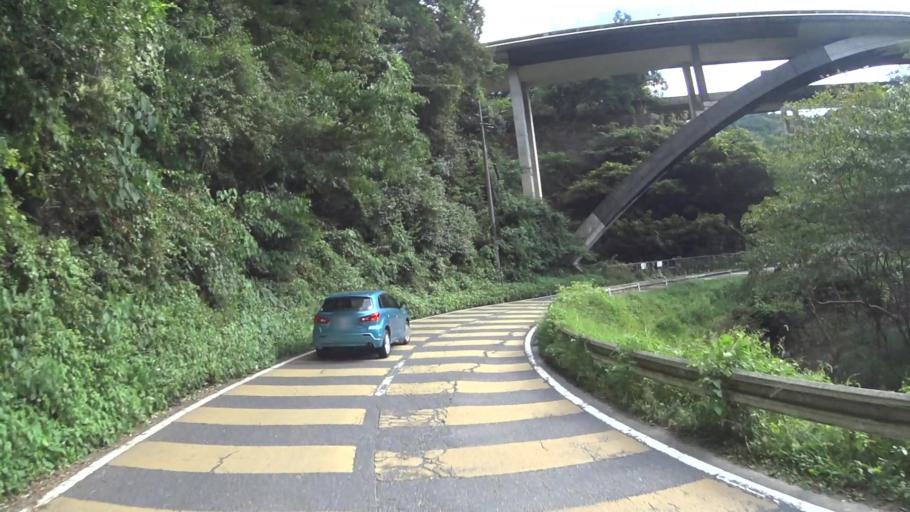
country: JP
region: Kyoto
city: Uji
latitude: 34.9152
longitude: 135.8629
